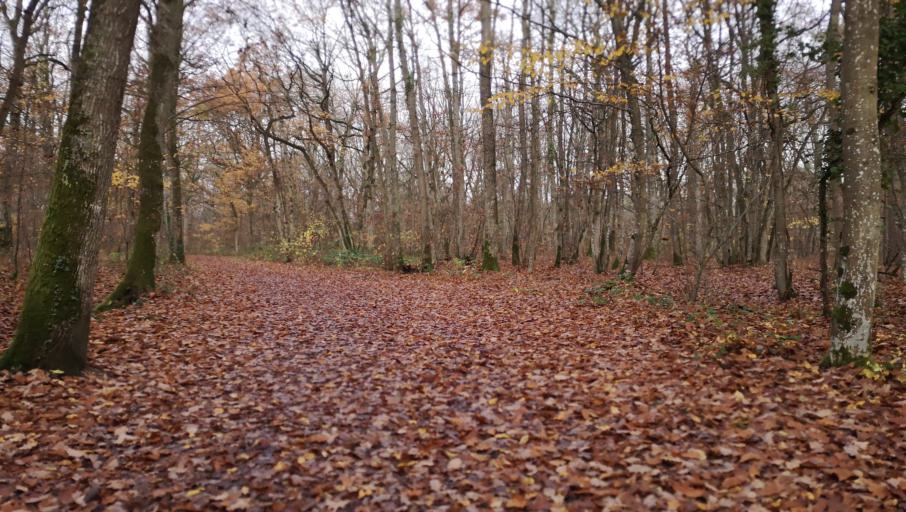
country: FR
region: Centre
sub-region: Departement du Loiret
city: Semoy
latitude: 47.9411
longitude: 1.9685
